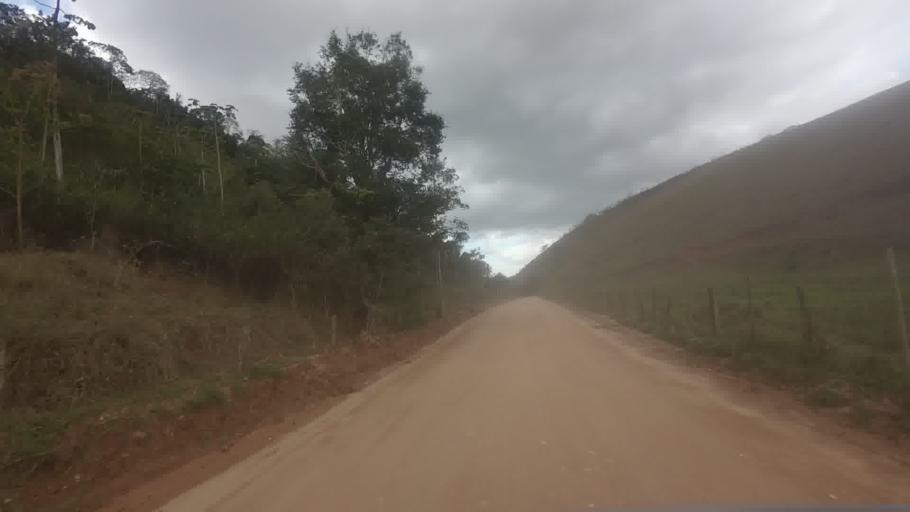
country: BR
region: Espirito Santo
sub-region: Mimoso Do Sul
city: Mimoso do Sul
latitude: -20.9460
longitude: -41.4143
